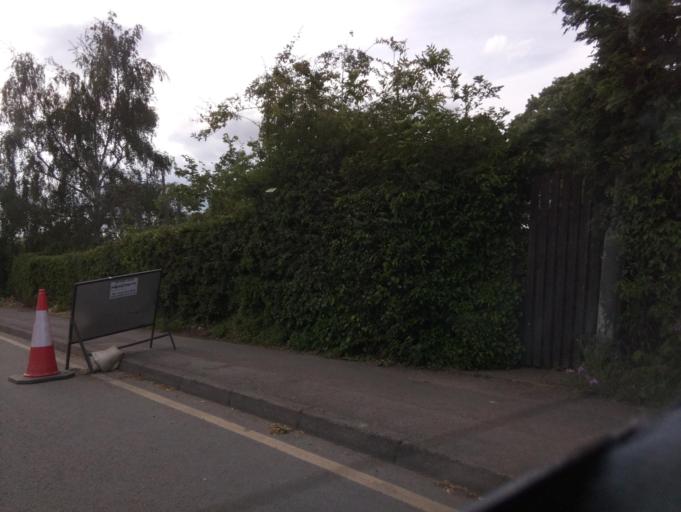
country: GB
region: England
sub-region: Worcestershire
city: Evesham
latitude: 52.0861
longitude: -1.9539
